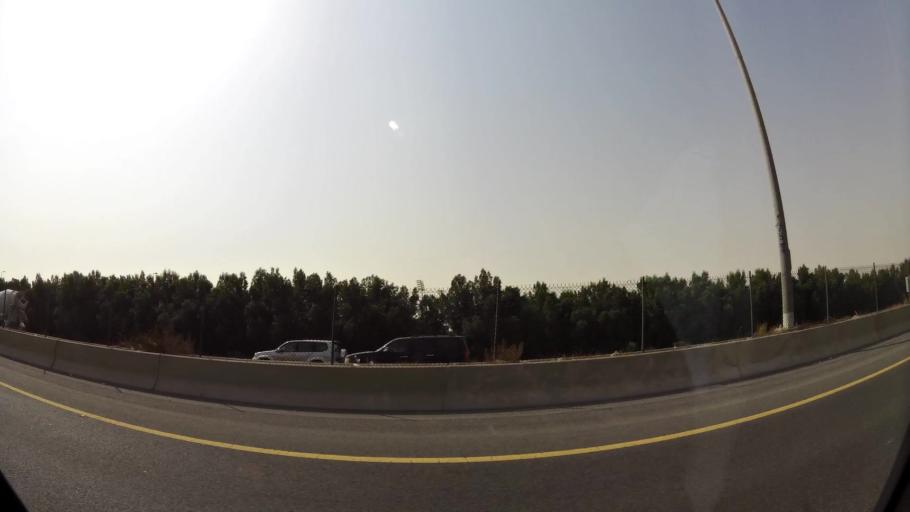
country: KW
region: Muhafazat al Jahra'
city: Al Jahra'
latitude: 29.3483
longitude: 47.6968
